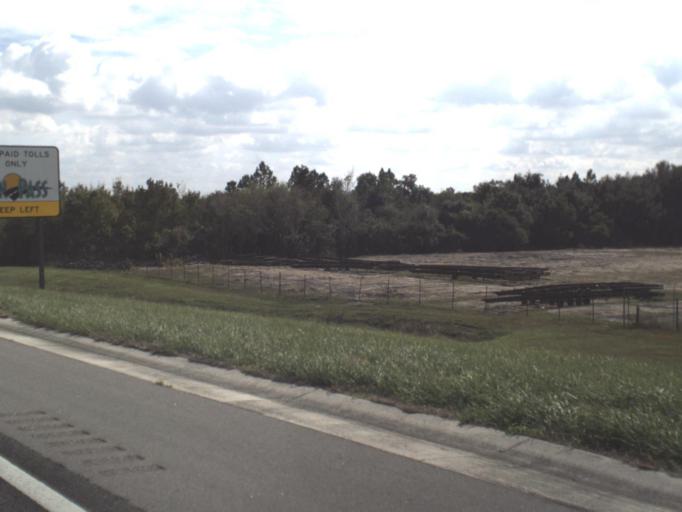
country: US
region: Florida
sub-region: Polk County
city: Crystal Lake
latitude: 28.0088
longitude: -81.8763
